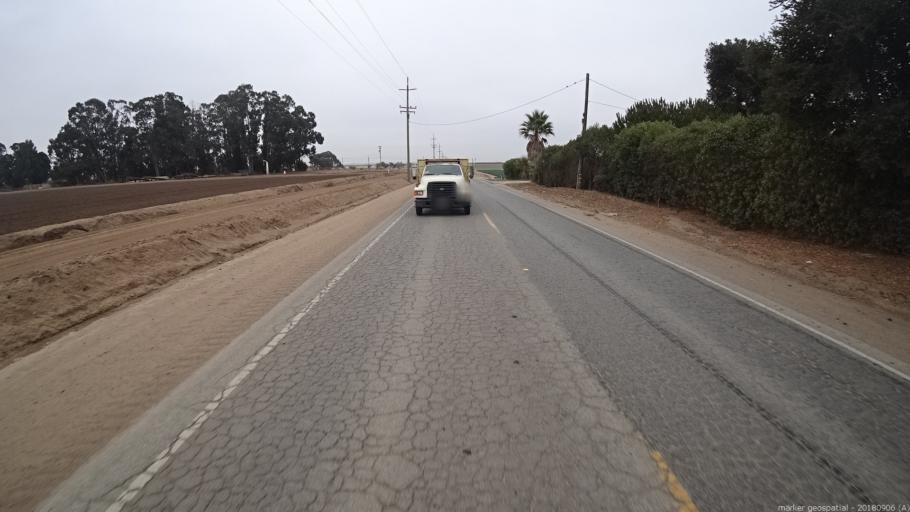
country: US
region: California
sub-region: Monterey County
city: Salinas
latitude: 36.6635
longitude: -121.5929
